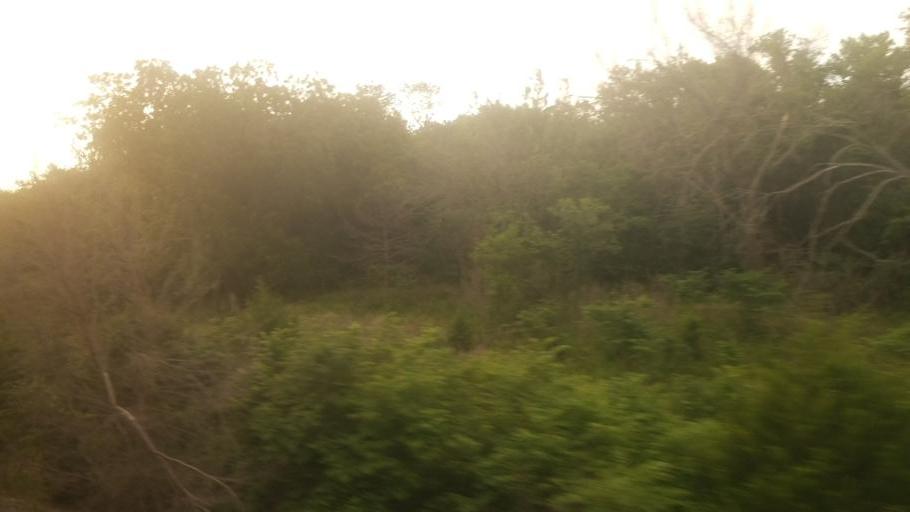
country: US
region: Kansas
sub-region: Osage County
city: Osage City
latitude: 38.5173
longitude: -95.9824
